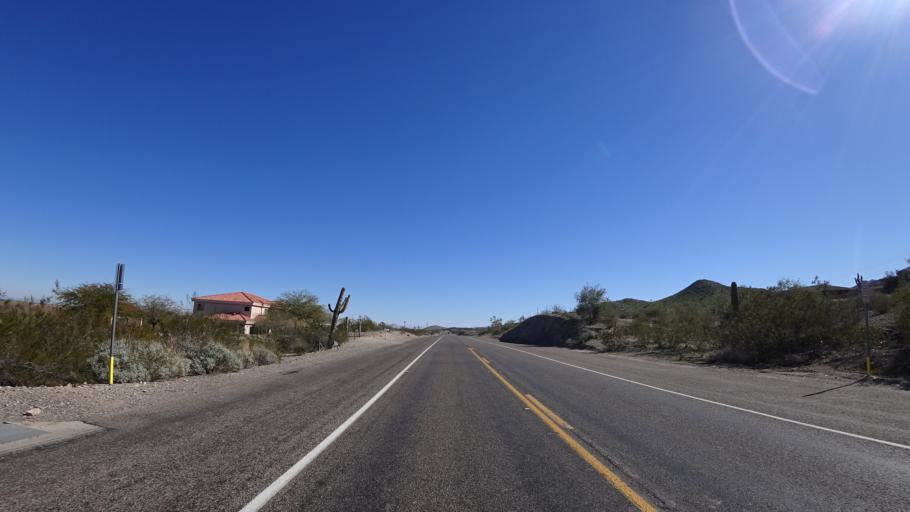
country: US
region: Arizona
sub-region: Maricopa County
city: Goodyear
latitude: 33.3755
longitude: -112.3574
